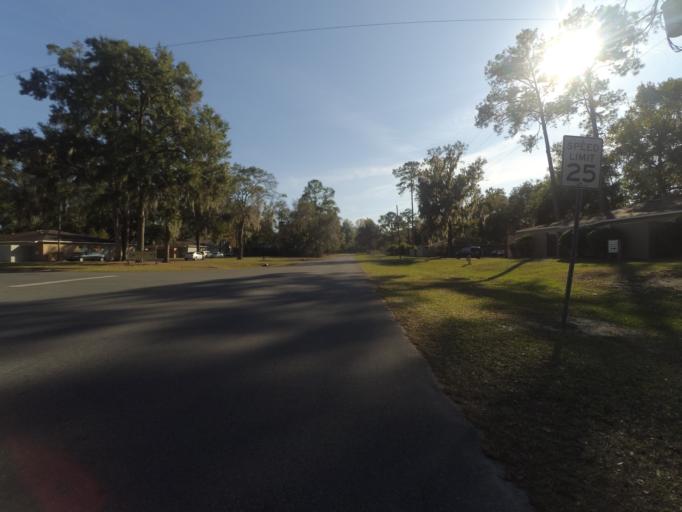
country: US
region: Florida
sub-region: Alachua County
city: Gainesville
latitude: 29.6168
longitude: -82.3674
